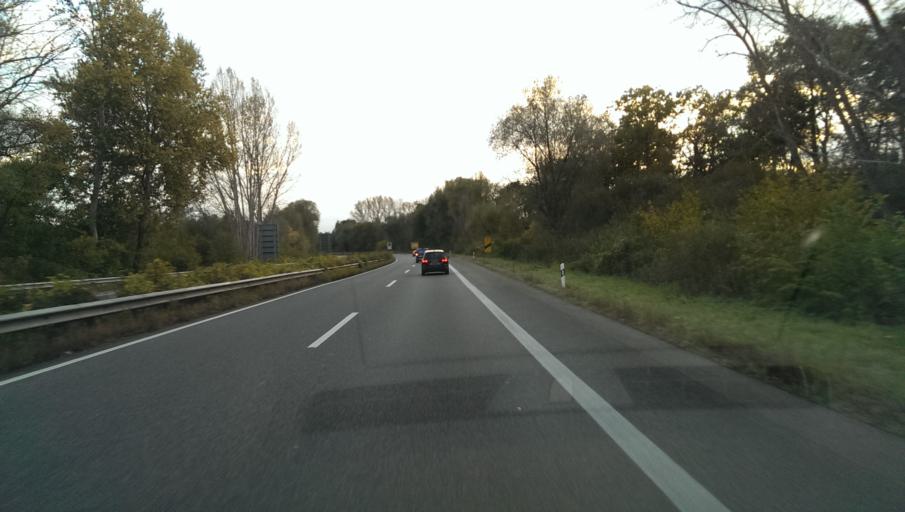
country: DE
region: Rheinland-Pfalz
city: Germersheim
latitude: 49.2282
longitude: 8.3569
